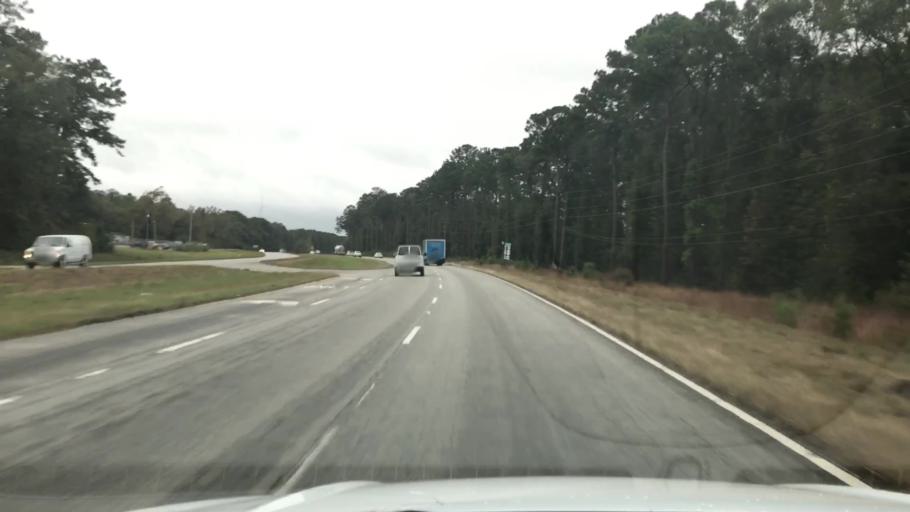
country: US
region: South Carolina
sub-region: Charleston County
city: Ravenel
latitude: 32.7600
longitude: -80.3886
